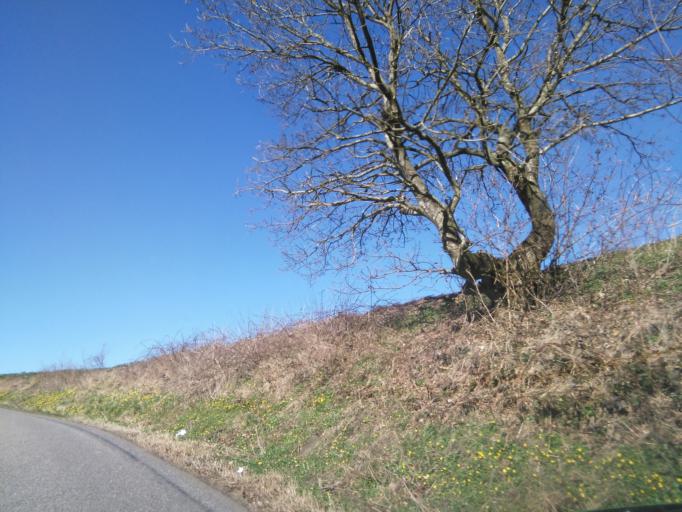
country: DK
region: Central Jutland
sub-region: Skanderborg Kommune
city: Stilling
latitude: 56.0934
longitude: 9.9761
